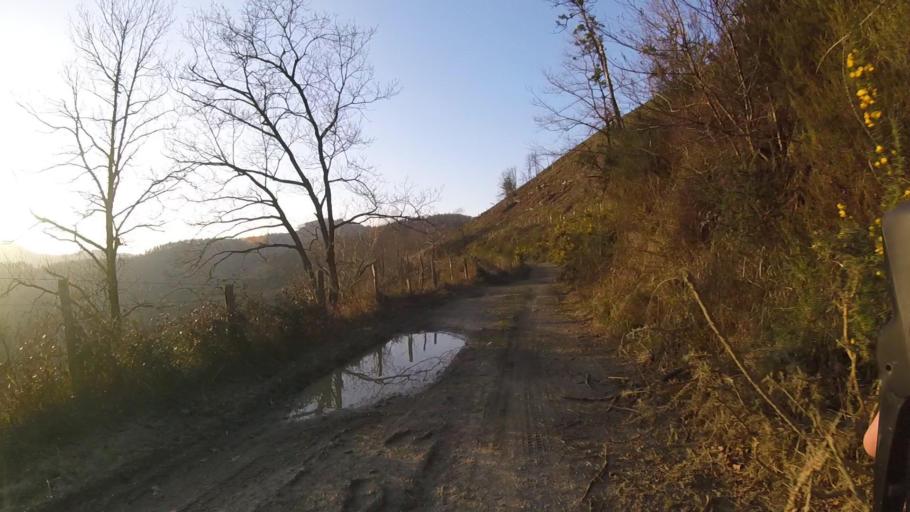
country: ES
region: Navarre
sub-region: Provincia de Navarra
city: Arano
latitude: 43.2484
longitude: -1.8570
